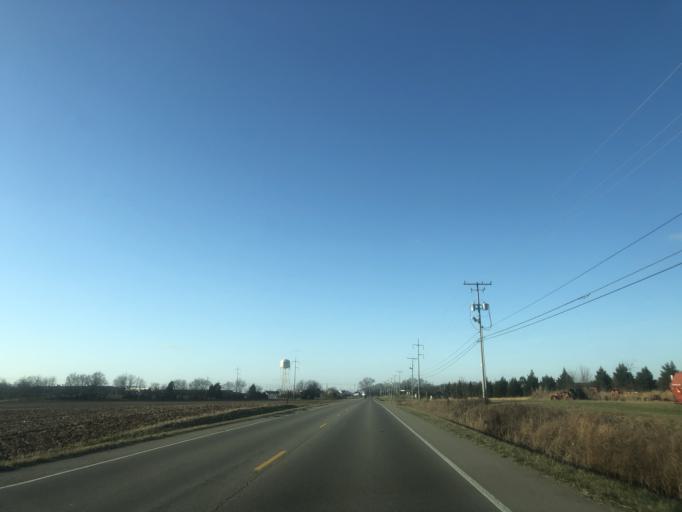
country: US
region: Tennessee
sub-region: Sumner County
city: Portland
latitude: 36.6281
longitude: -86.5597
